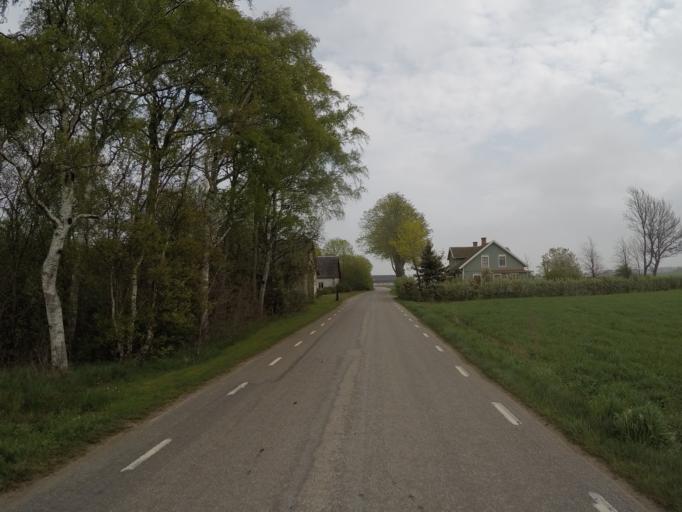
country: SE
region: Halland
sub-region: Laholms Kommun
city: Laholm
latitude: 56.5241
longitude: 13.0262
